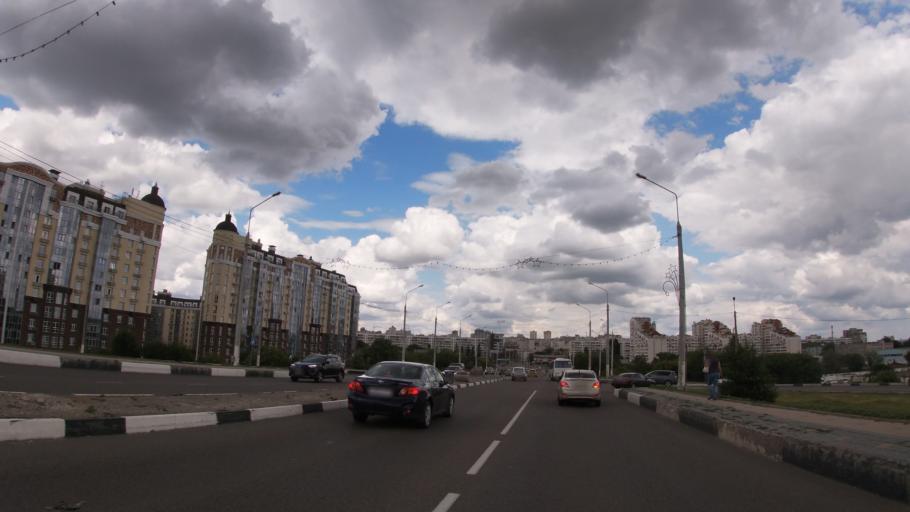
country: RU
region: Belgorod
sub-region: Belgorodskiy Rayon
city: Belgorod
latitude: 50.5878
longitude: 36.5885
